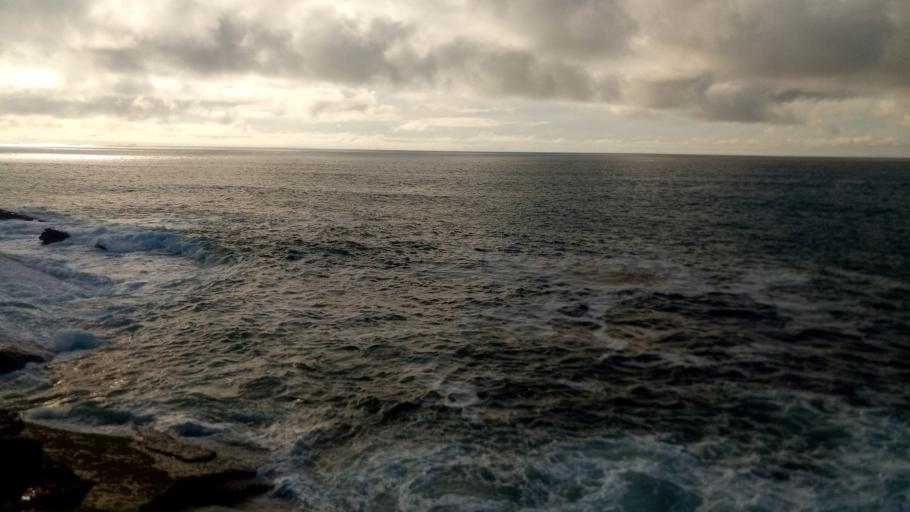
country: PT
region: Leiria
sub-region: Caldas da Rainha
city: Caldas da Rainha
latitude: 39.4957
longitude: -9.1748
